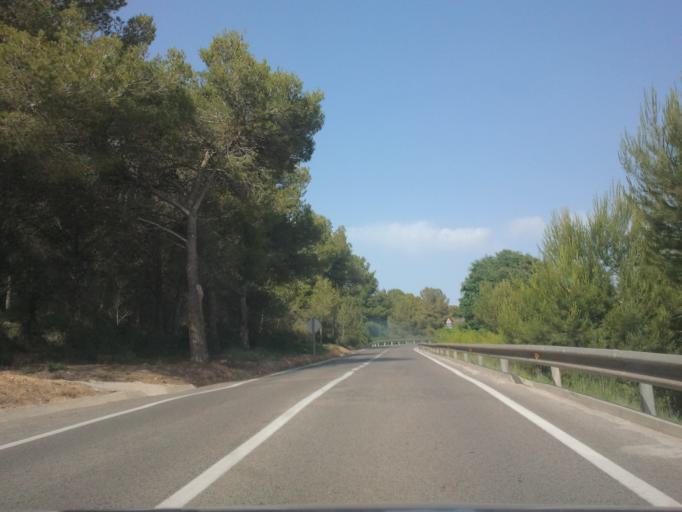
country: ES
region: Catalonia
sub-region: Provincia de Barcelona
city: Cubelles
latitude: 41.2283
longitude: 1.6801
